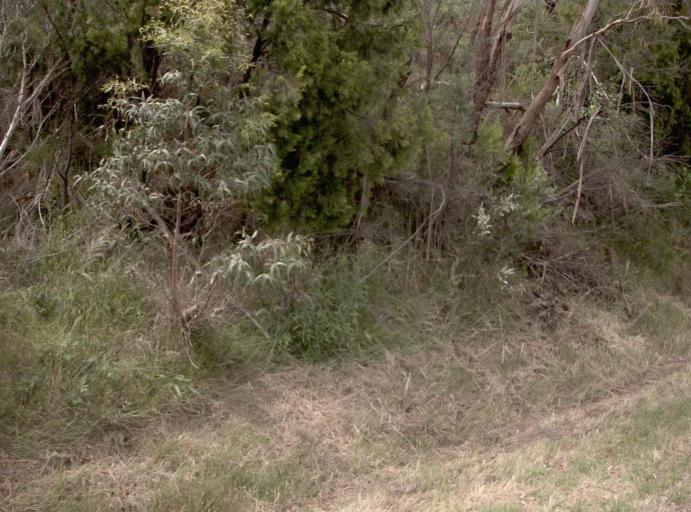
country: AU
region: Victoria
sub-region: Mornington Peninsula
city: McCrae
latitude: -38.3534
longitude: 144.9486
